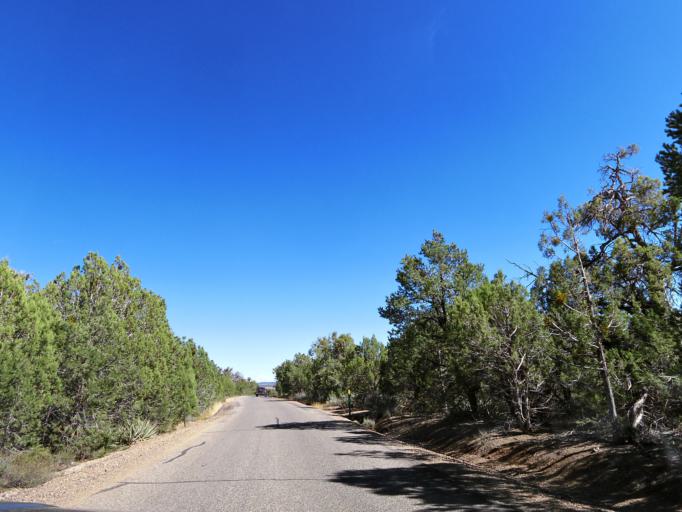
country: US
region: Colorado
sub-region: Montezuma County
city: Cortez
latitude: 37.1625
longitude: -108.4810
